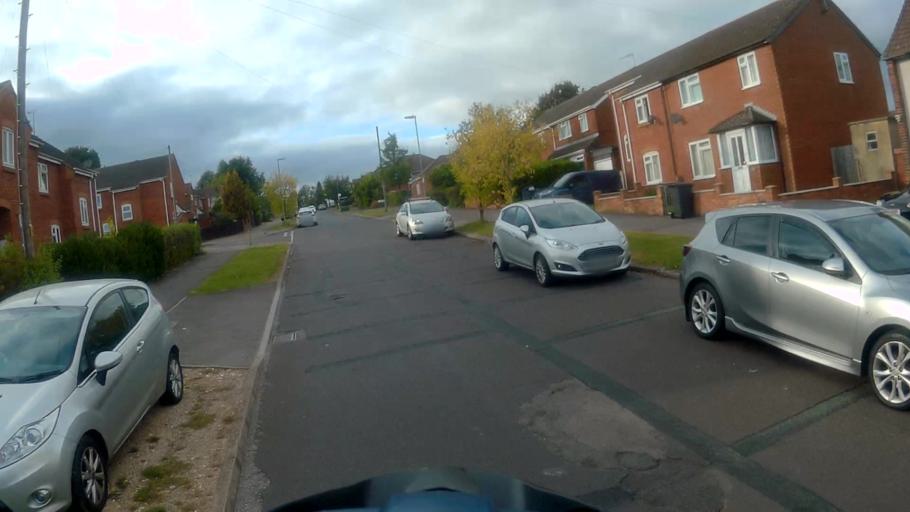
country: GB
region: England
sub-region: Hampshire
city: Basingstoke
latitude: 51.2552
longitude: -1.1072
